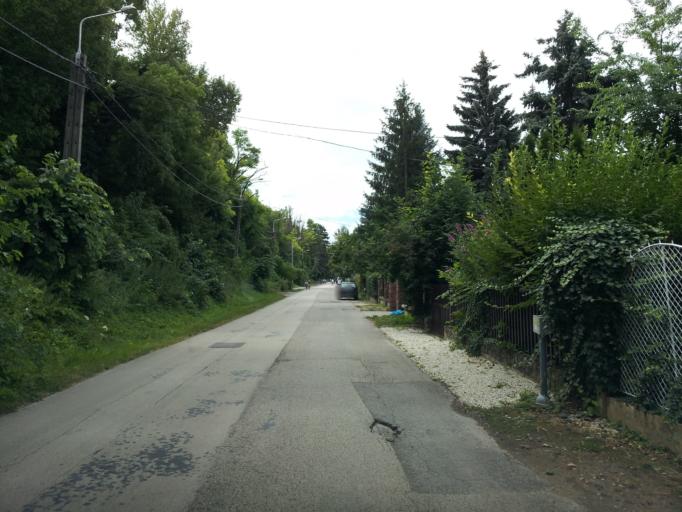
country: HU
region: Somogy
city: Balatonszabadi
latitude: 46.9689
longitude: 18.1600
